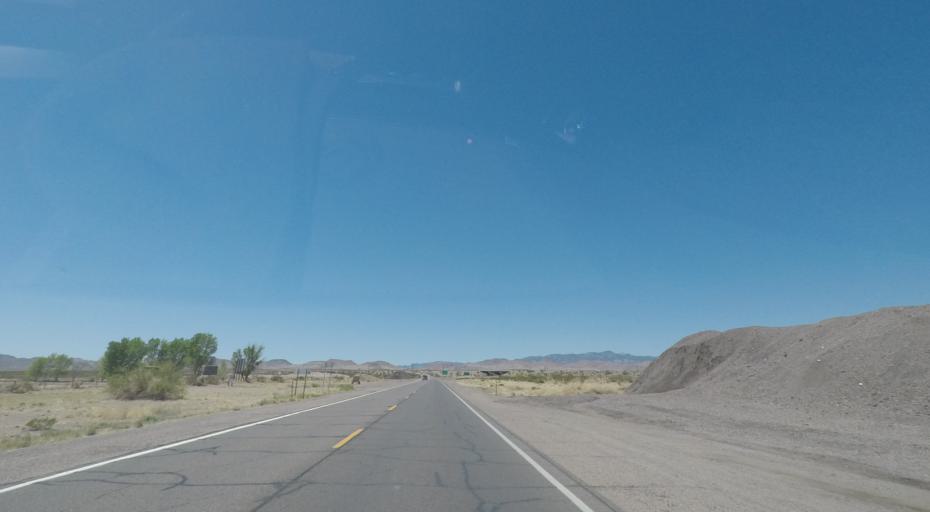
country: US
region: New Mexico
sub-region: Socorro County
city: Socorro
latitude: 33.9175
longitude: -106.8721
